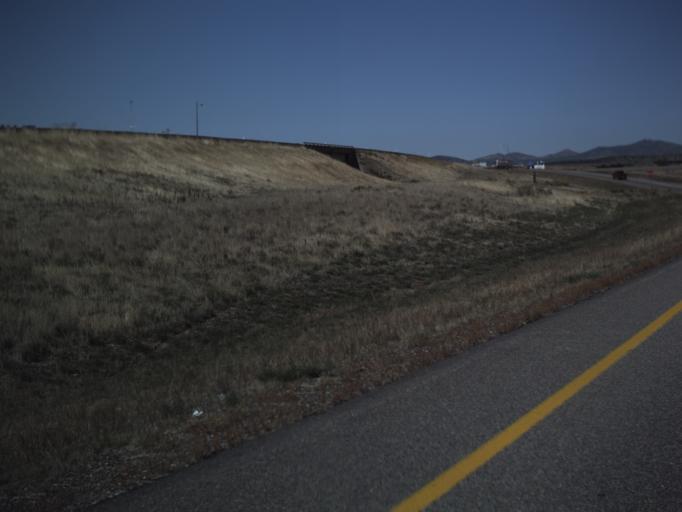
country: US
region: Utah
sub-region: Beaver County
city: Beaver
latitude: 38.2919
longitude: -112.6501
